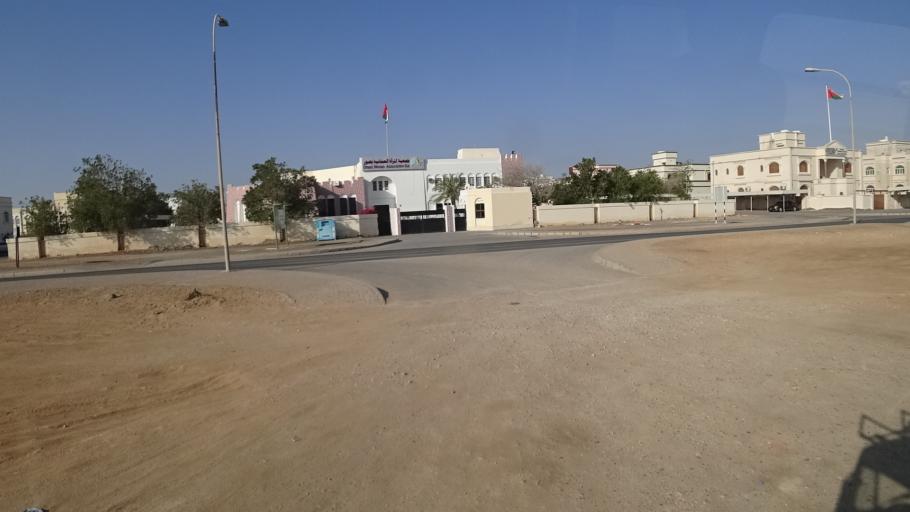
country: OM
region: Ash Sharqiyah
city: Sur
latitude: 22.5937
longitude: 59.4971
